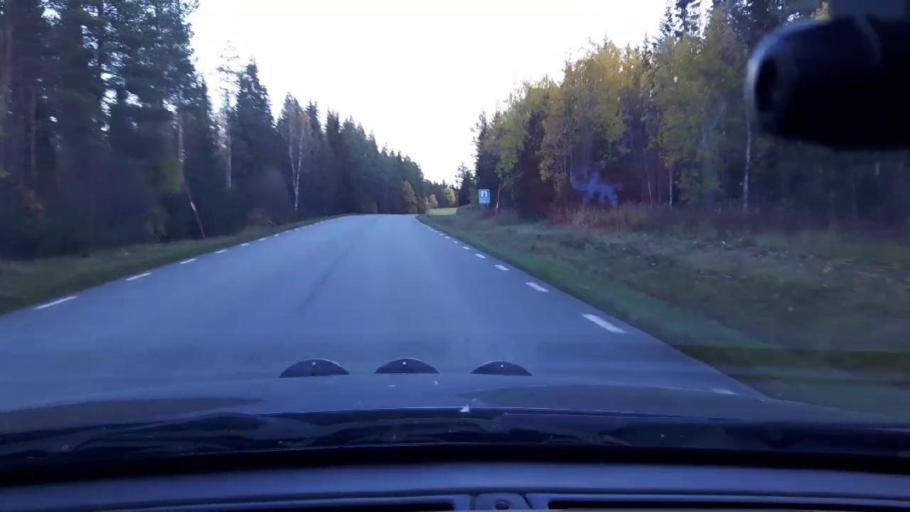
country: SE
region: Jaemtland
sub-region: Bergs Kommun
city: Hoverberg
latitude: 63.0436
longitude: 14.3382
